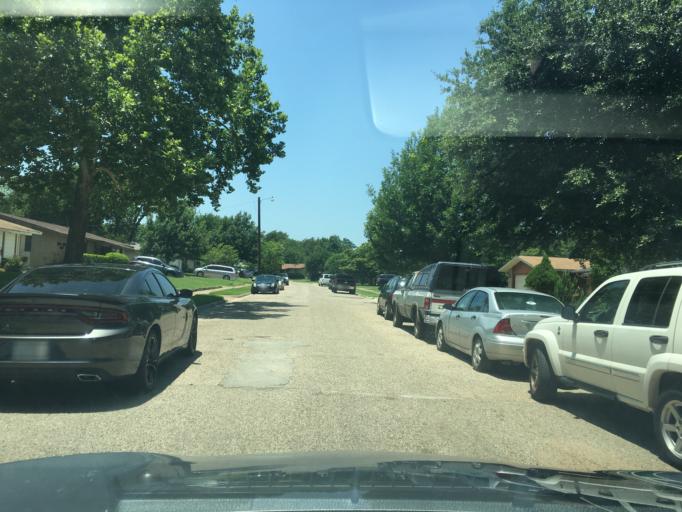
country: US
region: Texas
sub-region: Dallas County
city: Garland
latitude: 32.9133
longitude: -96.6848
